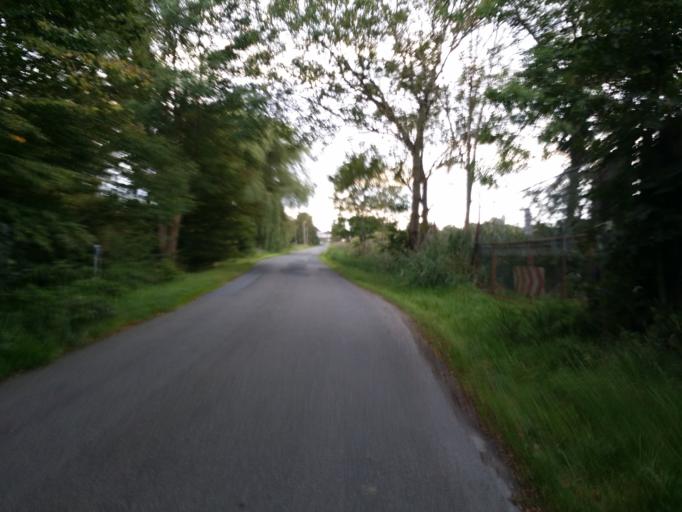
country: DE
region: Lower Saxony
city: Hemmoor
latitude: 53.7170
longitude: 9.1681
